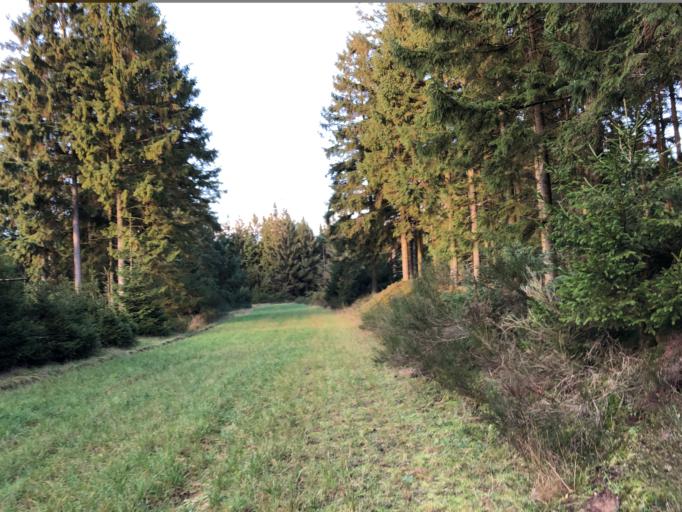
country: DK
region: Central Jutland
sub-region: Holstebro Kommune
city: Ulfborg
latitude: 56.2705
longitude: 8.3763
